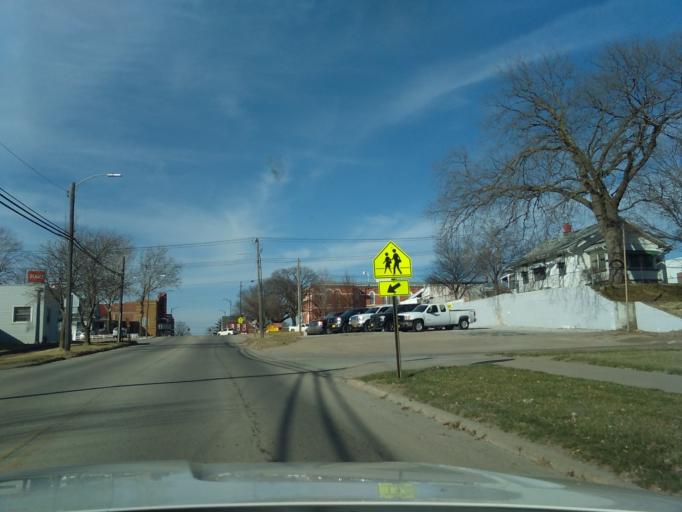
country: US
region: Nebraska
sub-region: Otoe County
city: Nebraska City
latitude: 40.6746
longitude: -95.8589
